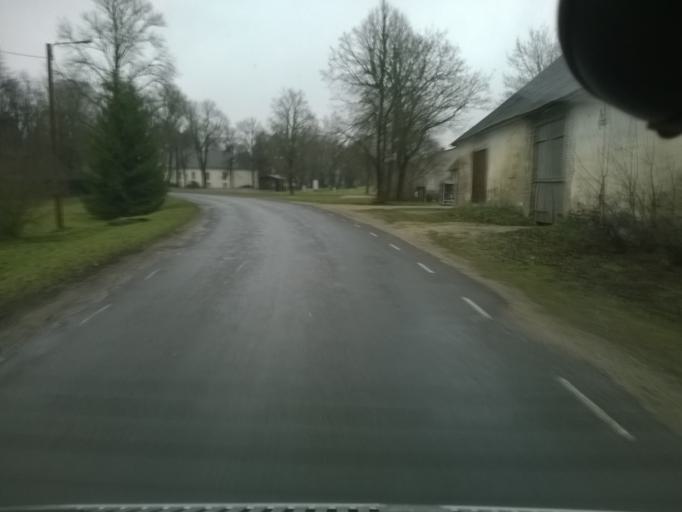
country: EE
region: Harju
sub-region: Nissi vald
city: Riisipere
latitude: 59.1269
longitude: 24.4679
